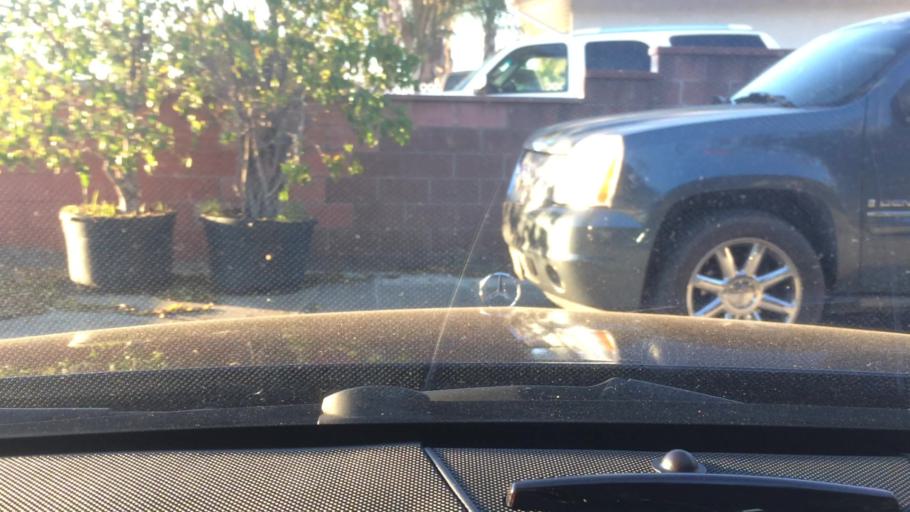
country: US
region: California
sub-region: Orange County
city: Anaheim
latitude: 33.8453
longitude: -117.8894
